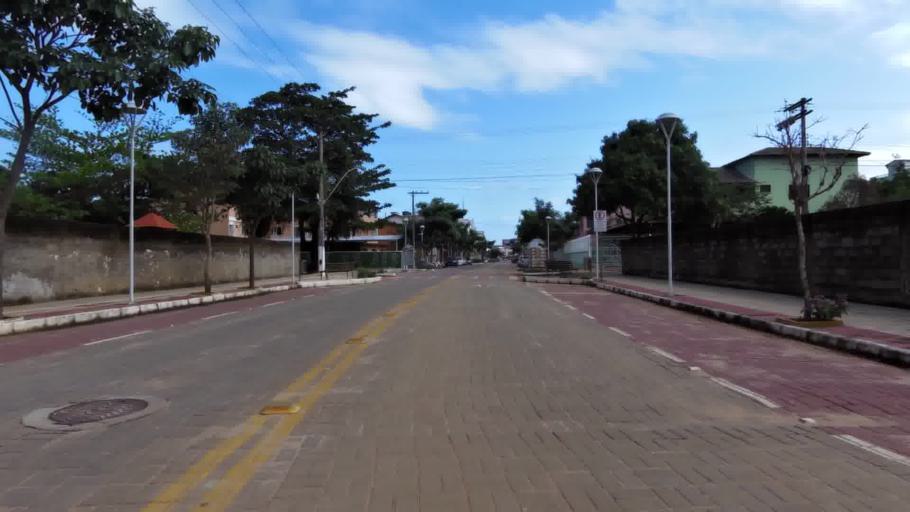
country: BR
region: Espirito Santo
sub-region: Piuma
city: Piuma
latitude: -20.8287
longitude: -40.6925
